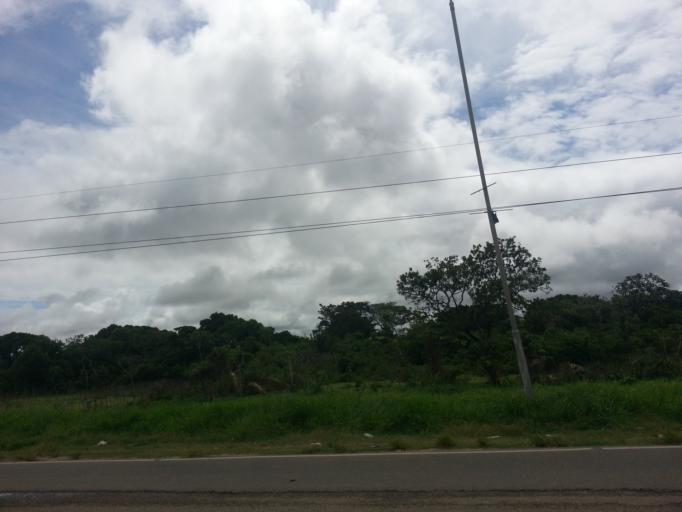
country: BO
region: Santa Cruz
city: La Belgica
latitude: -17.6551
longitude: -63.1577
